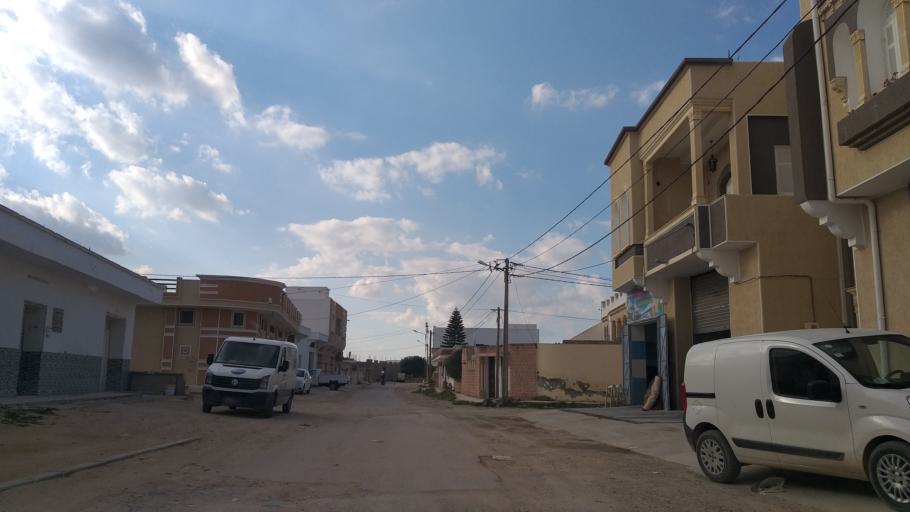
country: TN
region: Al Mahdiyah
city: El Jem
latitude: 35.3059
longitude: 10.7001
